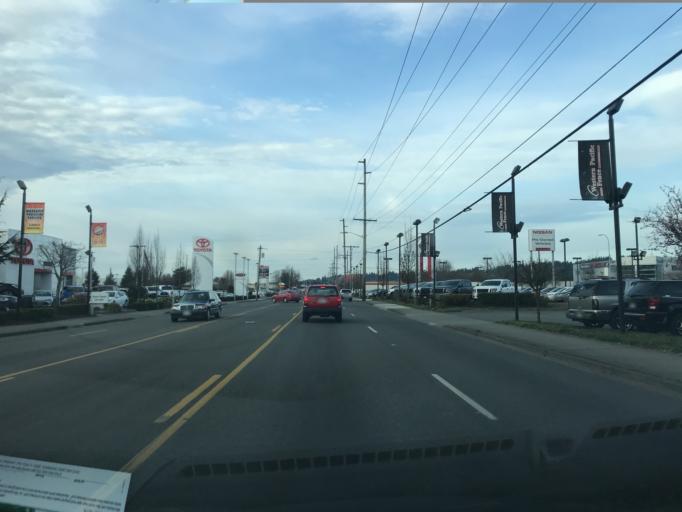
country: US
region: Washington
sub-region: King County
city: Auburn
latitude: 47.3375
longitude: -122.2223
